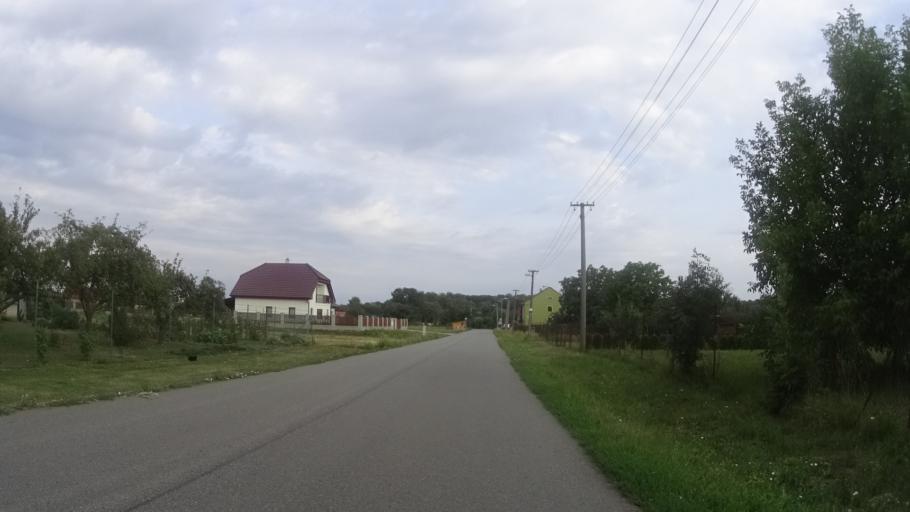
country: CZ
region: Zlin
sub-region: Okres Kromeriz
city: Kromeriz
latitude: 49.3146
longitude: 17.3900
